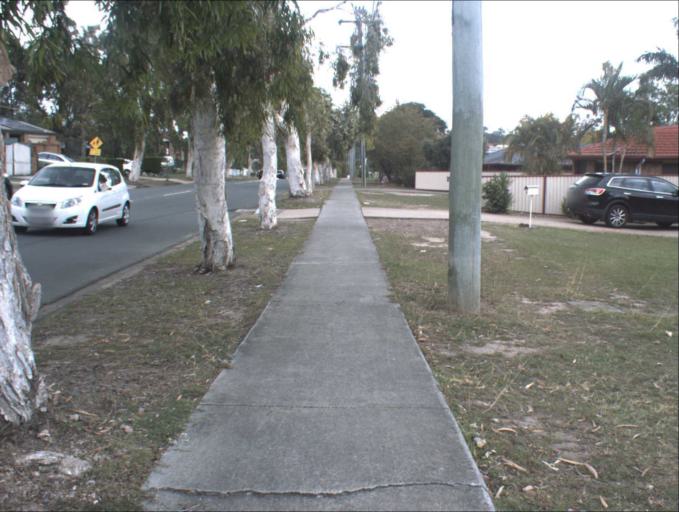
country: AU
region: Queensland
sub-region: Brisbane
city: Sunnybank Hills
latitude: -27.6668
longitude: 153.0378
